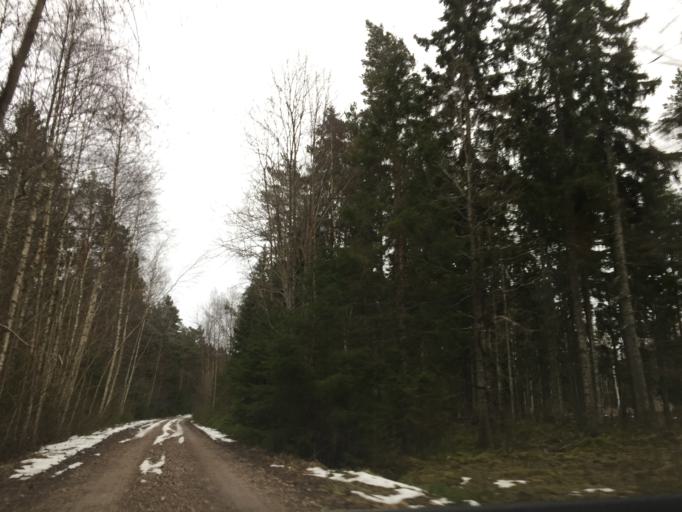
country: EE
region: Saare
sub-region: Kuressaare linn
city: Kuressaare
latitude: 58.4829
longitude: 22.2450
